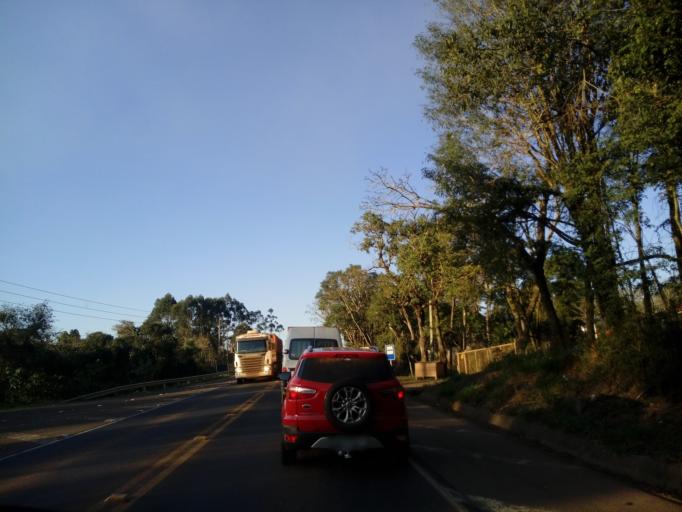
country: BR
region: Santa Catarina
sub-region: Chapeco
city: Chapeco
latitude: -27.2289
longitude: -52.6839
